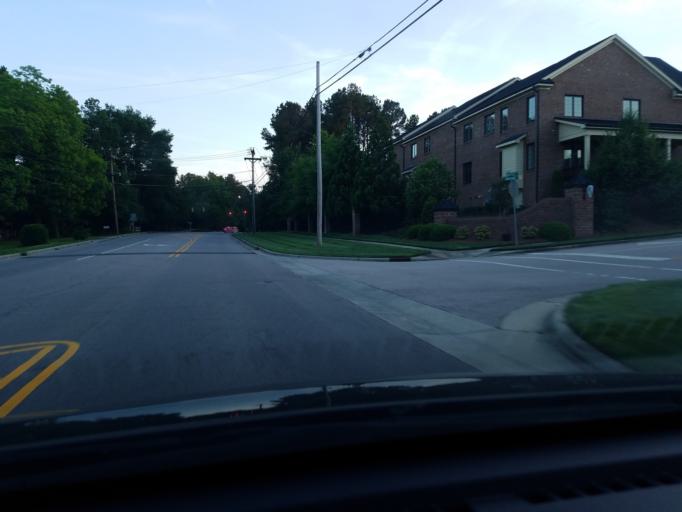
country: US
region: North Carolina
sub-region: Durham County
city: Durham
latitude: 35.9283
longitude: -78.9533
